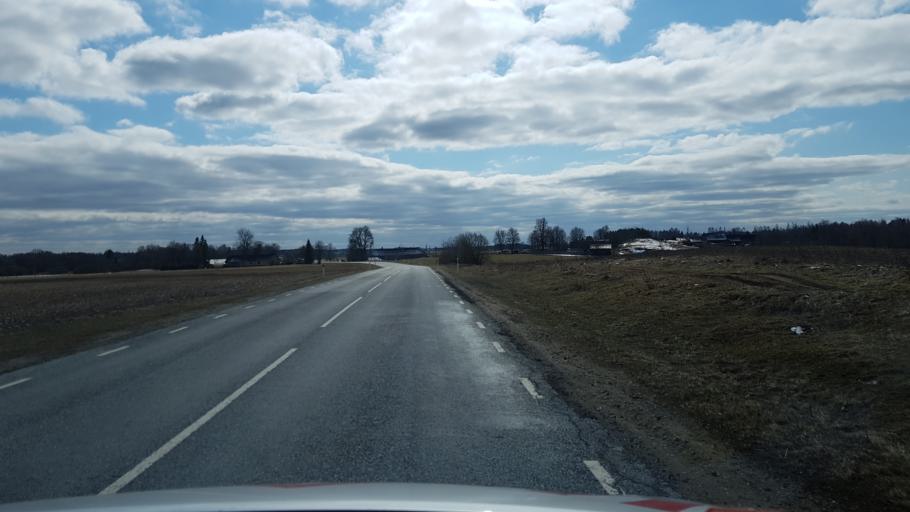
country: EE
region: Laeaene-Virumaa
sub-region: Tapa vald
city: Tapa
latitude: 59.3308
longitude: 26.0001
